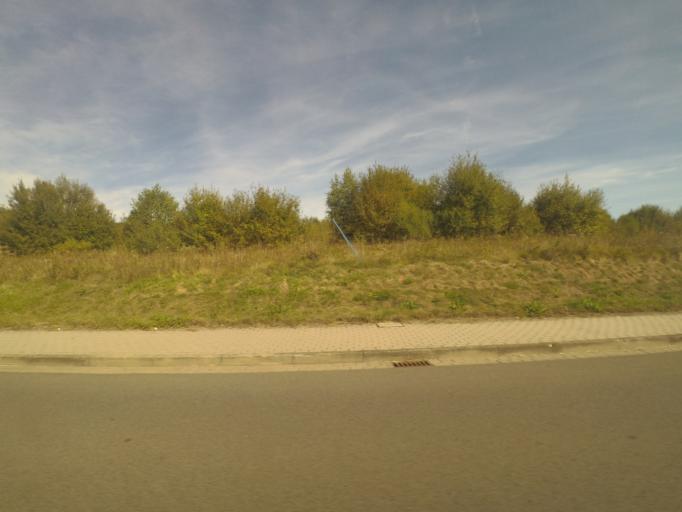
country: DE
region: Thuringia
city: Walldorf
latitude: 50.6190
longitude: 10.3908
